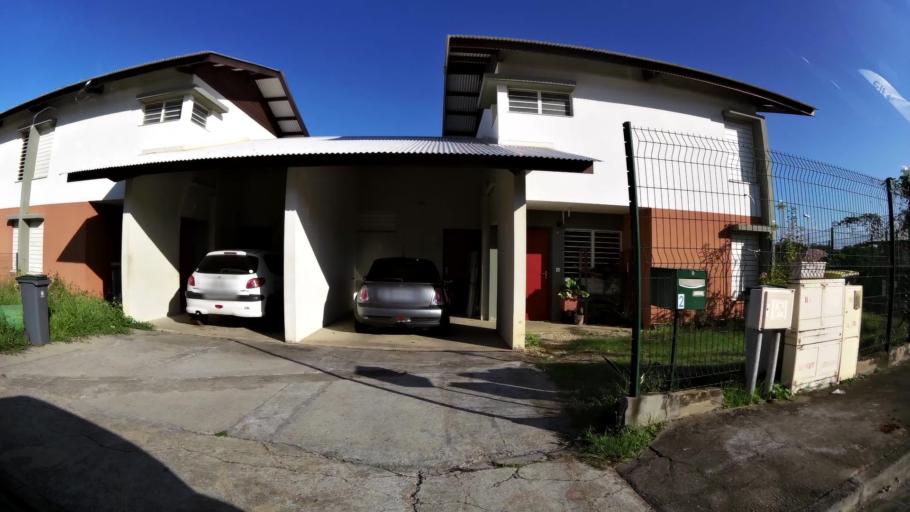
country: GF
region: Guyane
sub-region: Guyane
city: Remire-Montjoly
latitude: 4.8897
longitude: -52.2895
